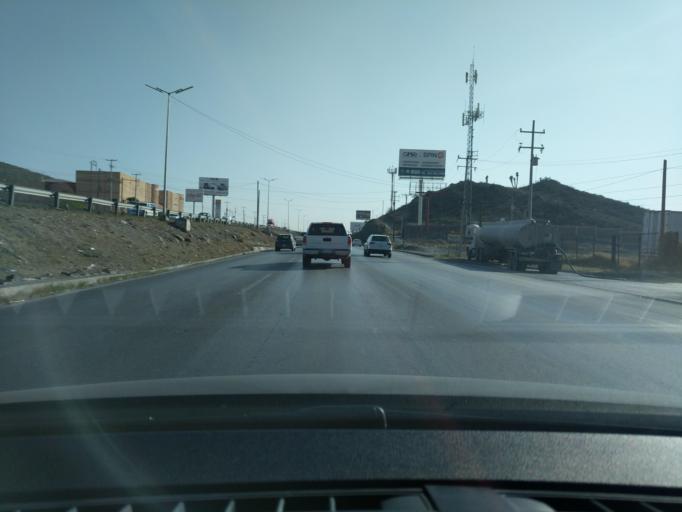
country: MX
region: Coahuila
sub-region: Ramos Arizpe
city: Ramos Arizpe
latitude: 25.5151
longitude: -100.9583
